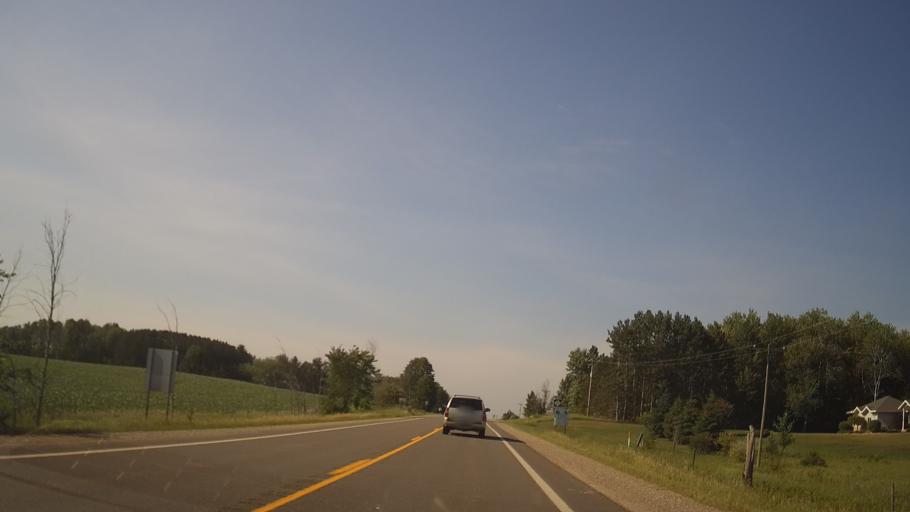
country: US
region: Michigan
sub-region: Ogemaw County
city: West Branch
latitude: 44.3355
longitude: -84.1257
